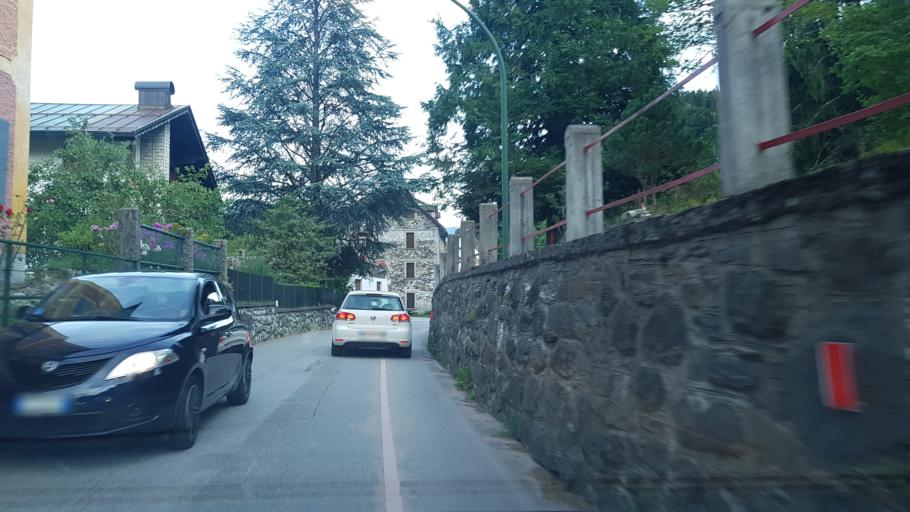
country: IT
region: Friuli Venezia Giulia
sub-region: Provincia di Udine
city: Rigolato
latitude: 46.5488
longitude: 12.8544
